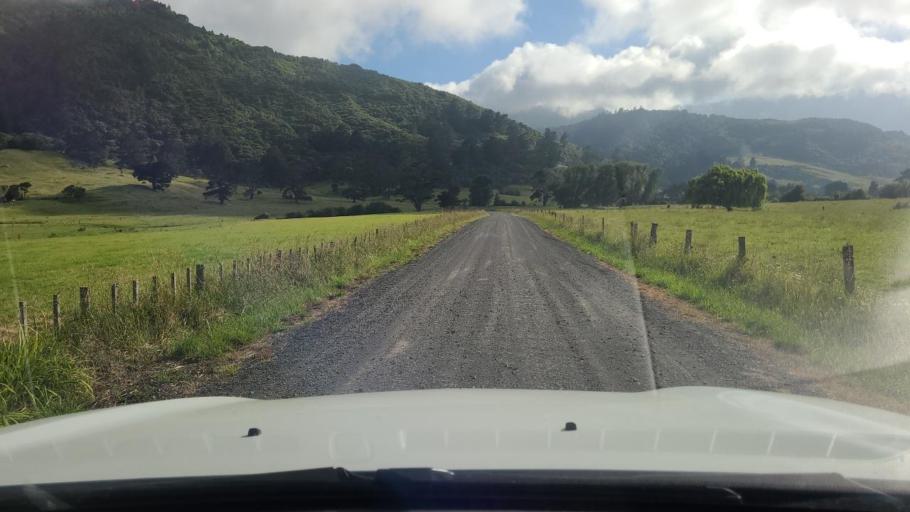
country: NZ
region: Bay of Plenty
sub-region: Western Bay of Plenty District
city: Katikati
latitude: -37.5639
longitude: 175.7418
